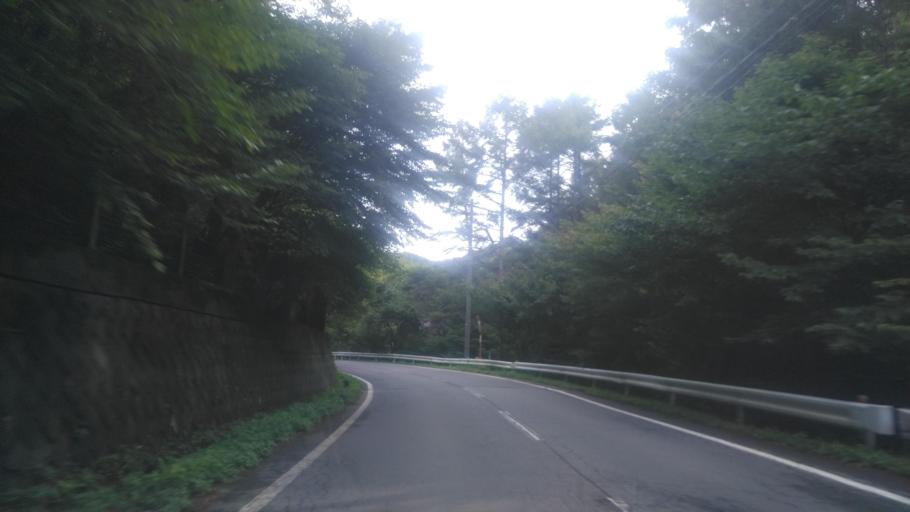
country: JP
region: Nagano
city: Ueda
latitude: 36.5002
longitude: 138.2298
